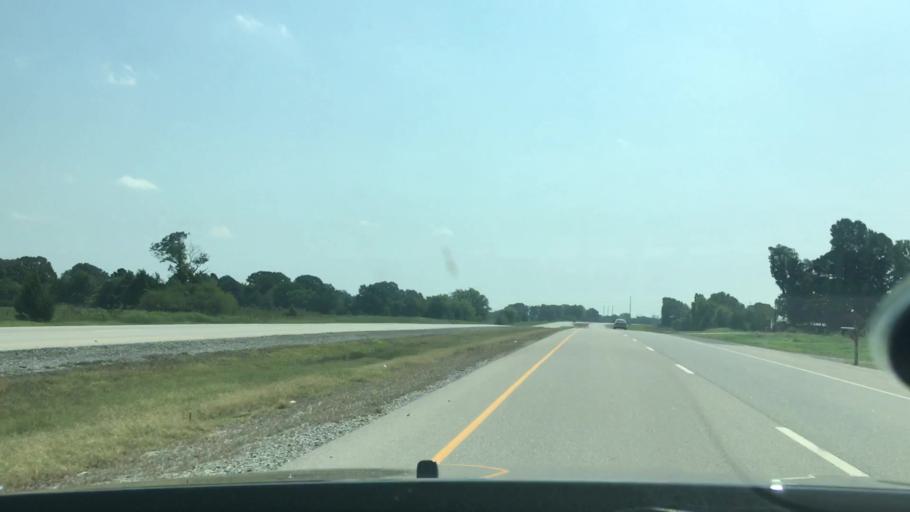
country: US
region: Oklahoma
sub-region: Atoka County
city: Atoka
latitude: 34.3384
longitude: -96.0624
